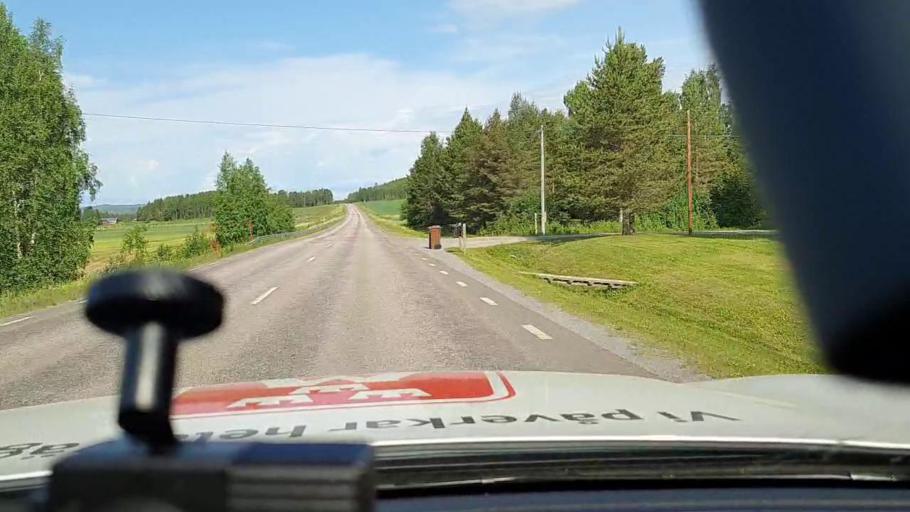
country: SE
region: Norrbotten
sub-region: Bodens Kommun
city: Boden
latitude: 65.9101
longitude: 21.3515
